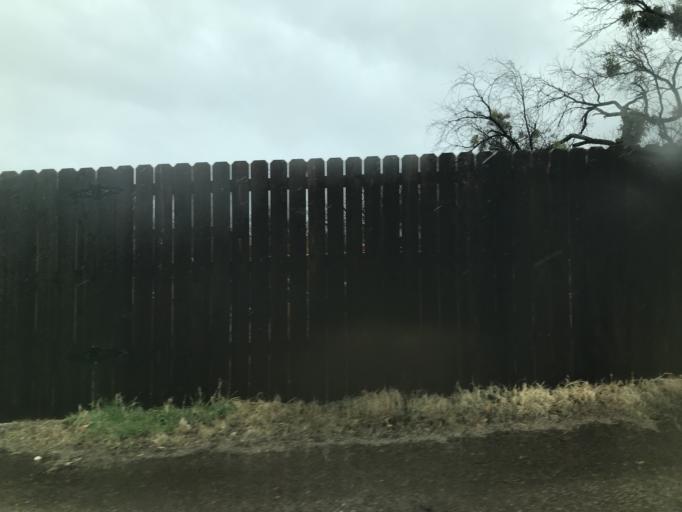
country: US
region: Texas
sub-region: Tom Green County
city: San Angelo
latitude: 31.4636
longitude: -100.4189
